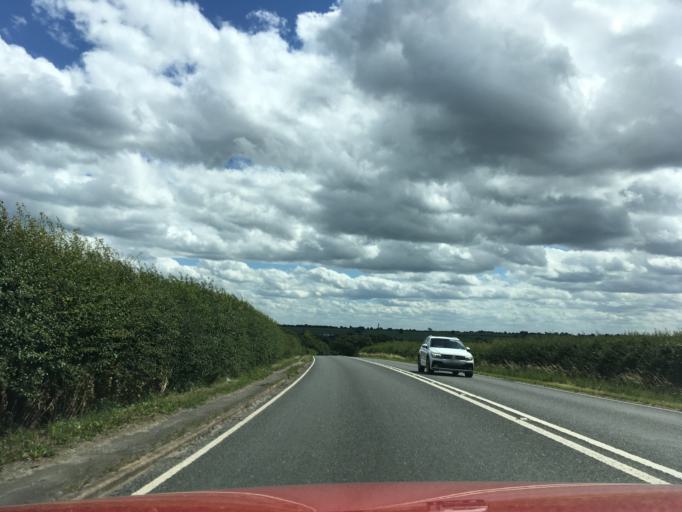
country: GB
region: England
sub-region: Nottinghamshire
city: East Leake
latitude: 52.8443
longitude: -1.1419
